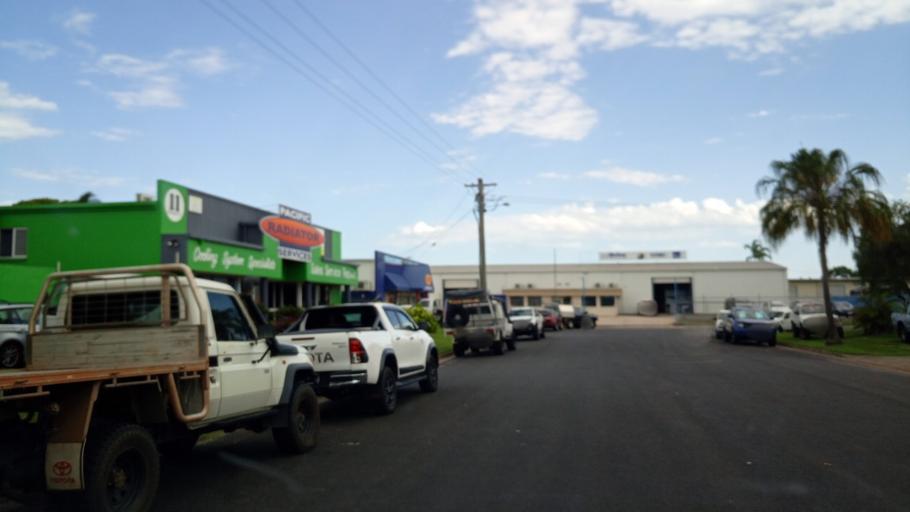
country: AU
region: Queensland
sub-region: Cairns
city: Cairns
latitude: -16.9356
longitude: 145.7590
